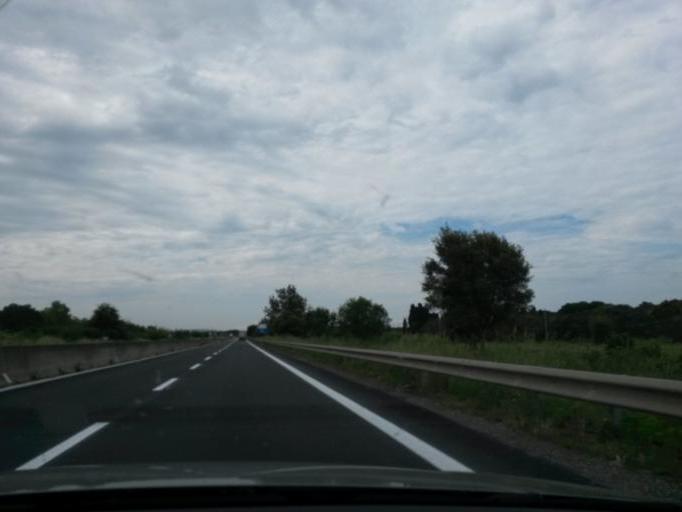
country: IT
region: Tuscany
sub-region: Provincia di Livorno
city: San Vincenzo
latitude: 43.1272
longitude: 10.5470
